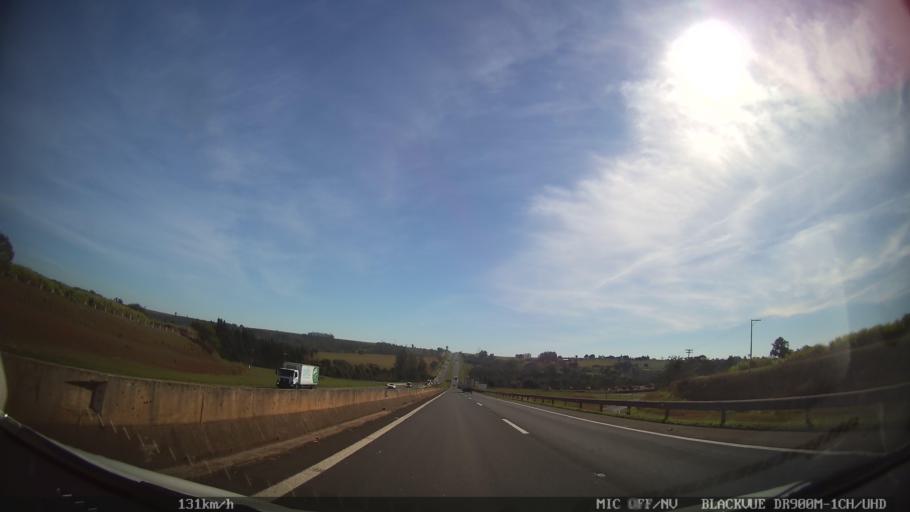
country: BR
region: Sao Paulo
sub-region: Leme
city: Leme
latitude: -22.1039
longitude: -47.4139
